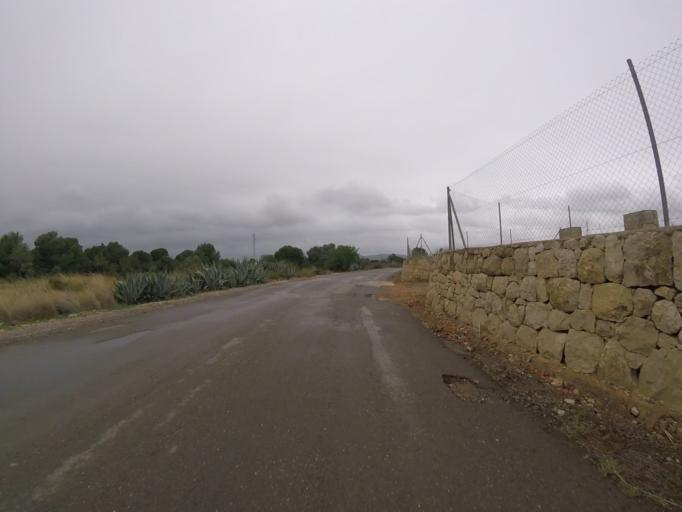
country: ES
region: Valencia
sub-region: Provincia de Castello
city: Alcoceber
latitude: 40.2389
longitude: 0.2499
